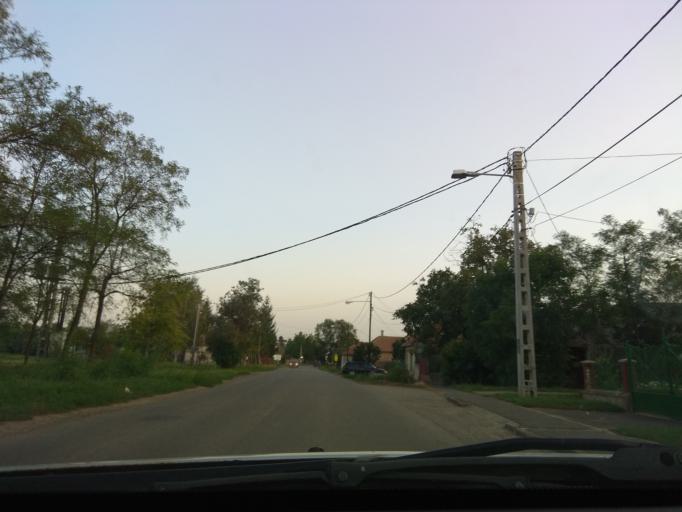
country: HU
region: Borsod-Abauj-Zemplen
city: Szerencs
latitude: 48.1936
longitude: 21.2149
